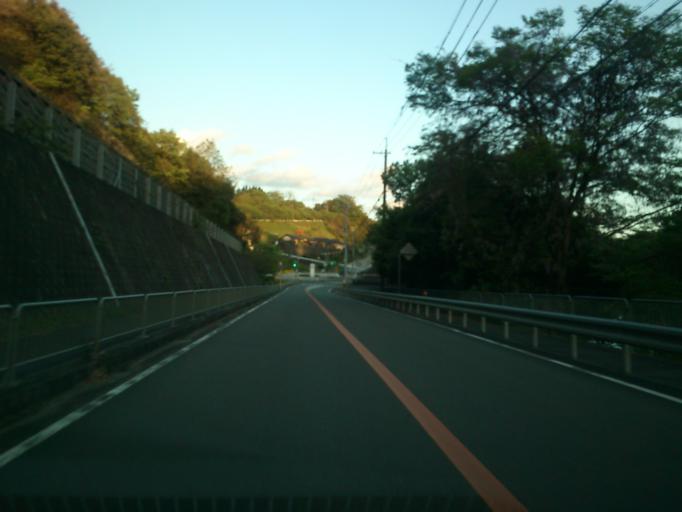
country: JP
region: Kyoto
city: Ayabe
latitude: 35.2148
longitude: 135.4228
